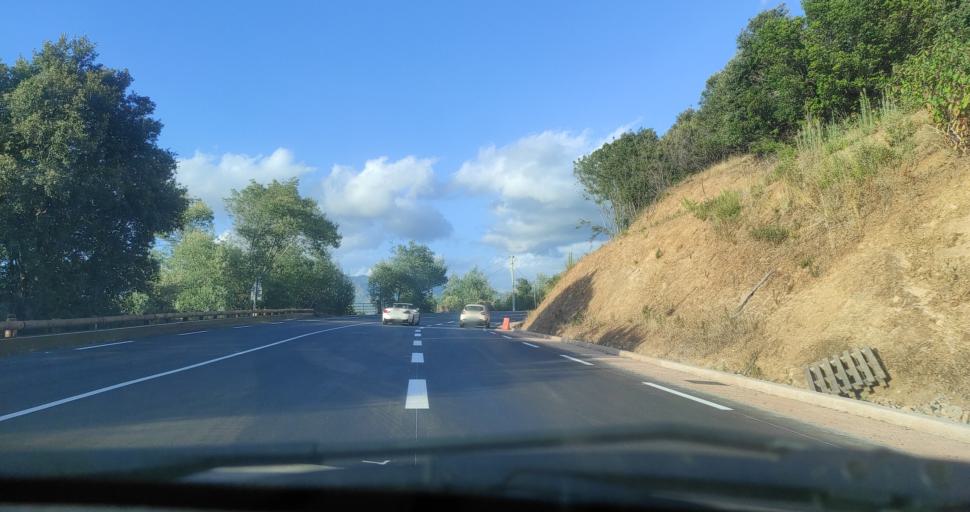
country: FR
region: Corsica
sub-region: Departement de la Corse-du-Sud
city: Appietto
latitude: 42.0340
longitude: 8.7579
